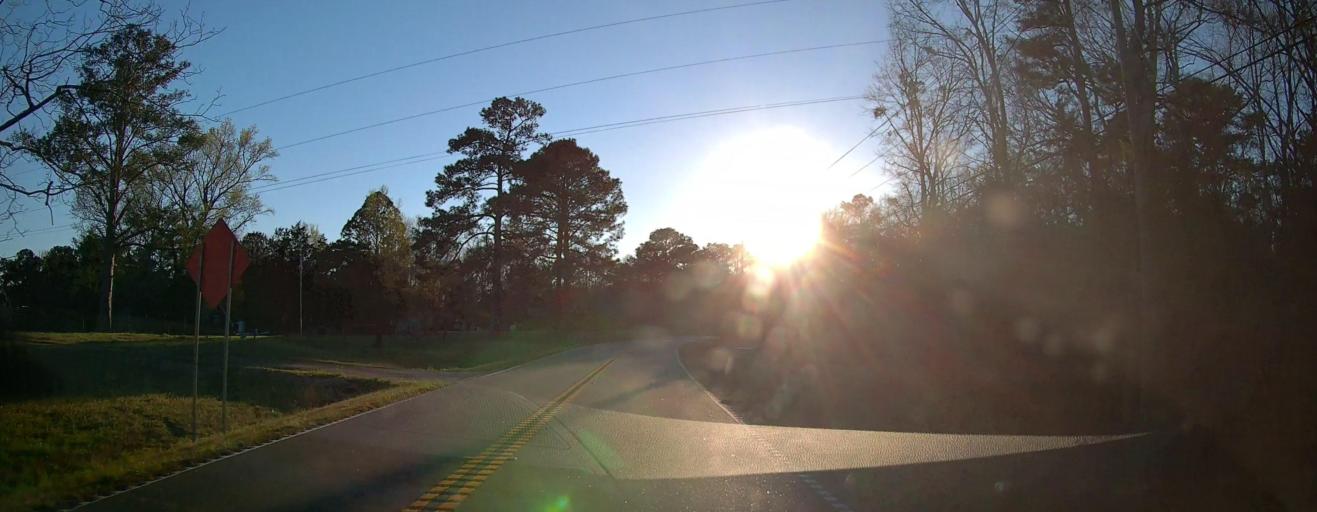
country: US
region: Georgia
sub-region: Harris County
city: Hamilton
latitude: 32.6552
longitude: -84.8573
